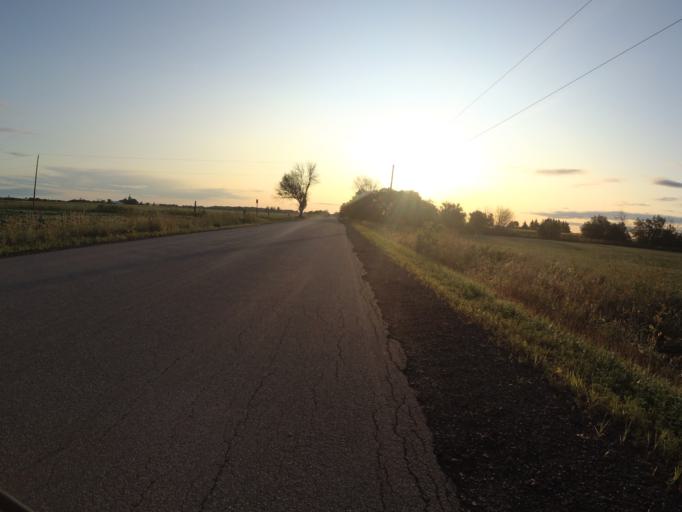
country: CA
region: Ontario
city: Ottawa
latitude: 45.1301
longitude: -75.4853
